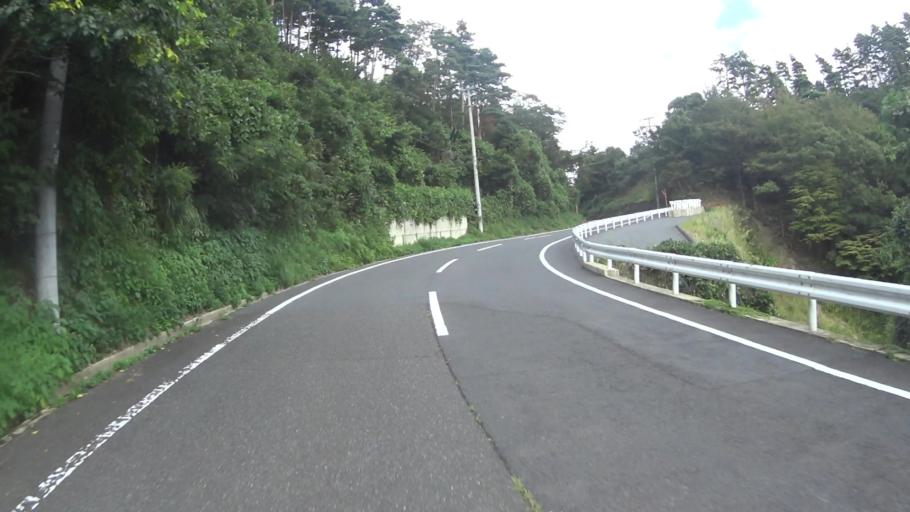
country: JP
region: Kyoto
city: Miyazu
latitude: 35.7327
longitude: 135.1781
